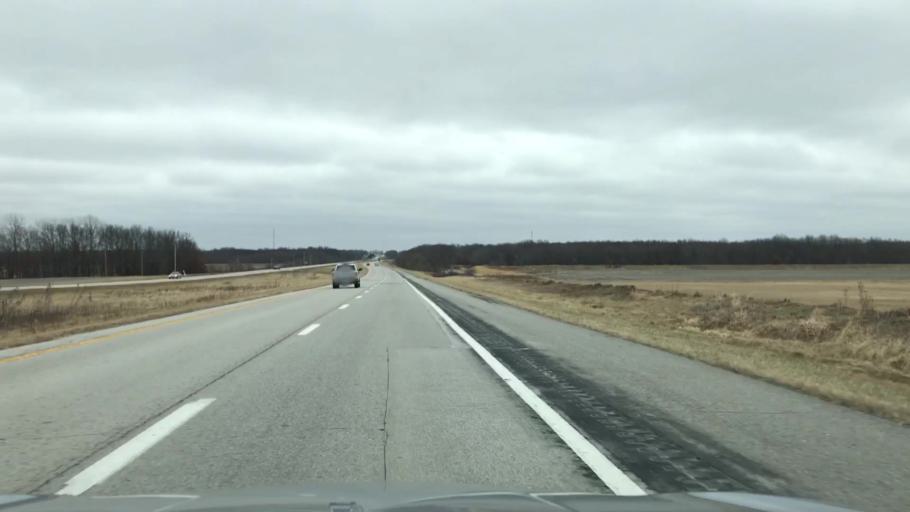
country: US
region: Missouri
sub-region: Linn County
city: Linneus
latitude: 39.7773
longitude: -93.3384
